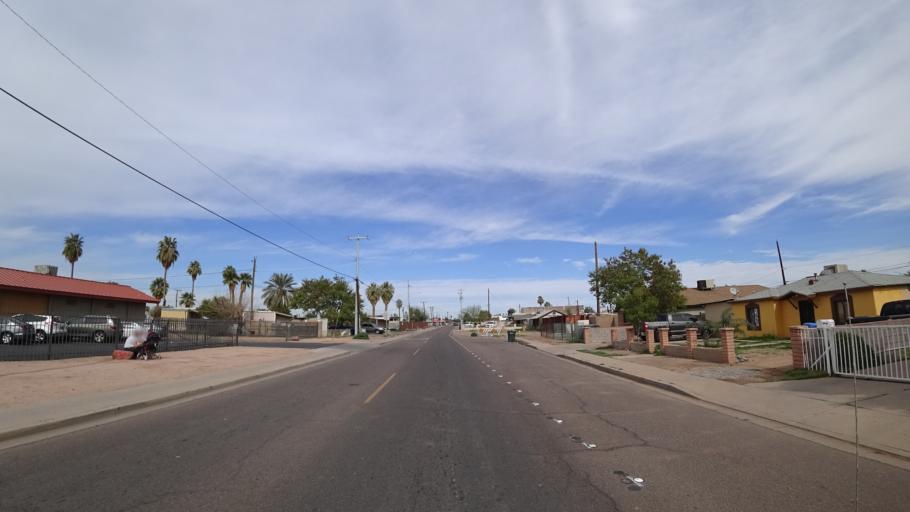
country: US
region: Arizona
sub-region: Maricopa County
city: Phoenix
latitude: 33.4490
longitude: -112.1260
